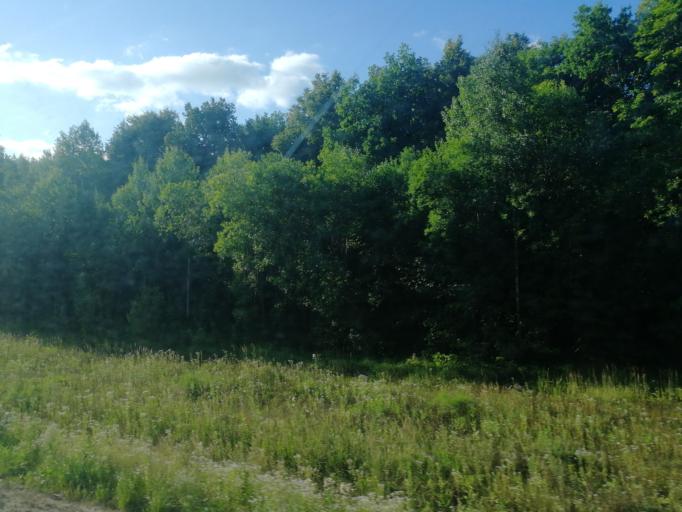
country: RU
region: Tula
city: Novogurovskiy
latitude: 54.2790
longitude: 37.2369
